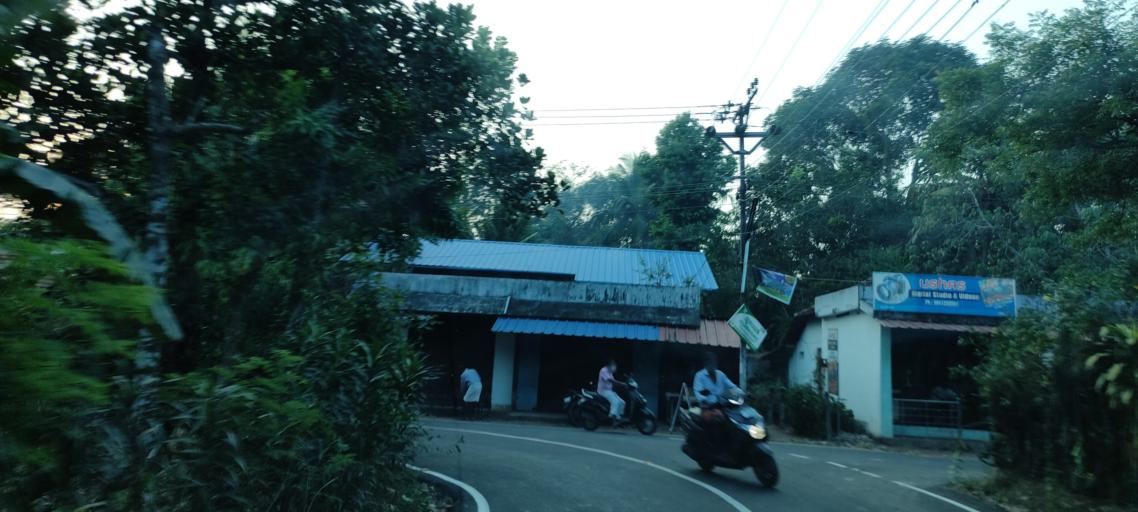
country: IN
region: Kerala
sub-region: Alappuzha
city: Mavelikara
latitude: 9.2697
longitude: 76.5485
